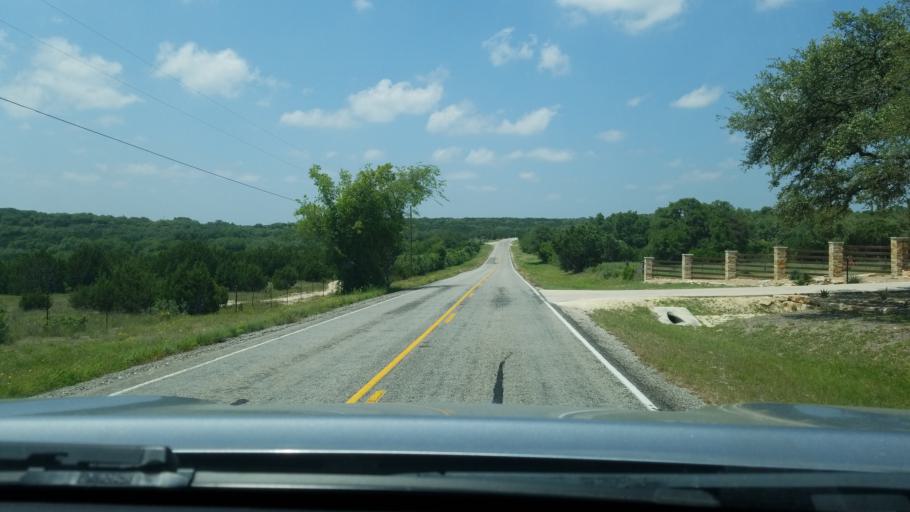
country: US
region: Texas
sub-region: Hays County
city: Woodcreek
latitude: 30.0650
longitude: -98.2150
